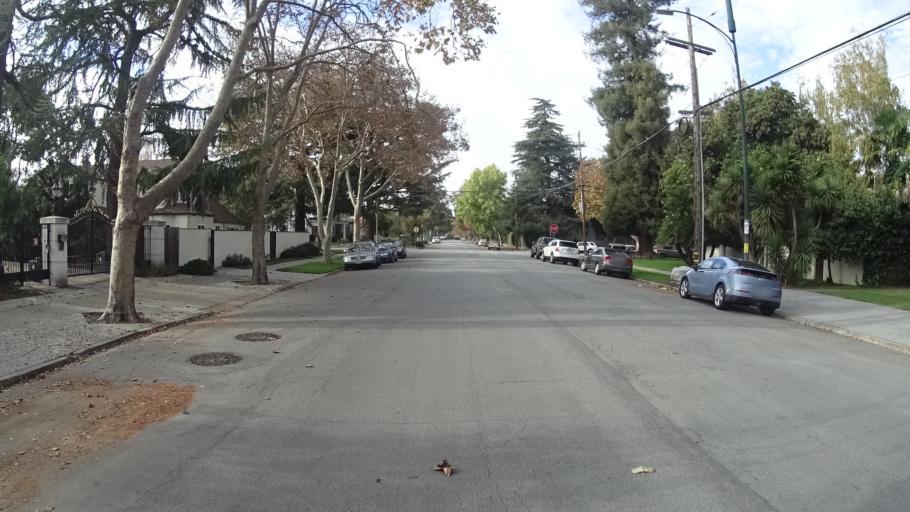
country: US
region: California
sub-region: Santa Clara County
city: Burbank
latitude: 37.3382
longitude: -121.9229
